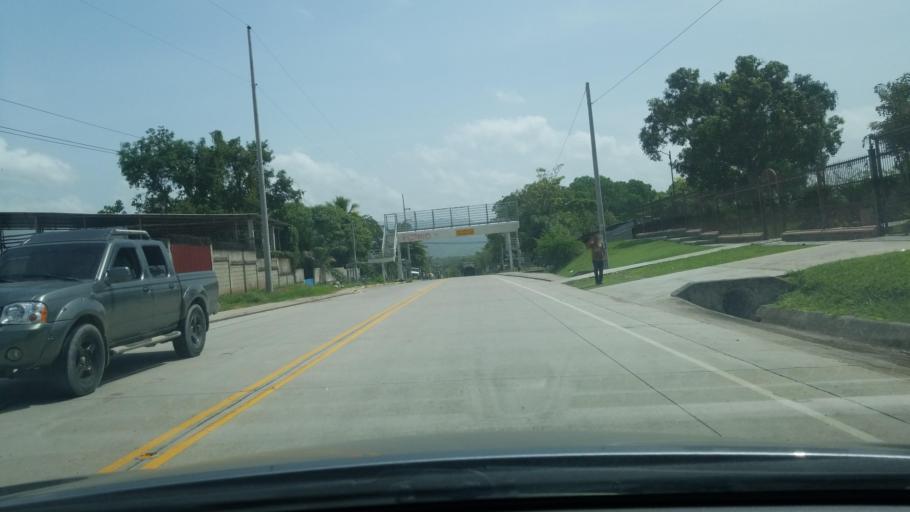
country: HN
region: Copan
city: Florida
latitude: 15.0246
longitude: -88.8325
